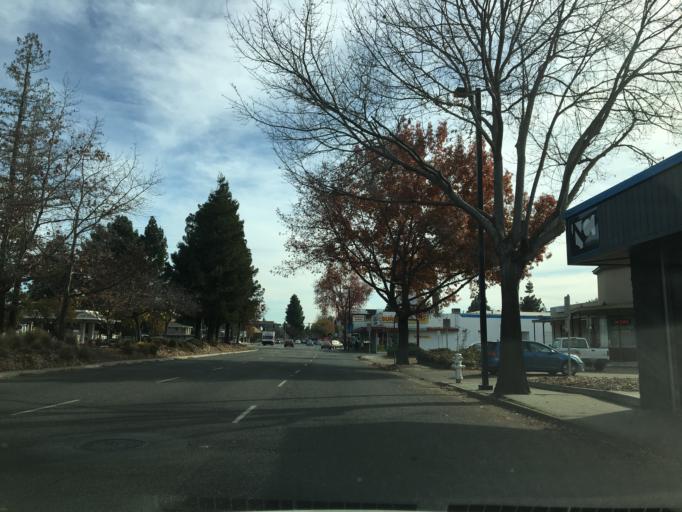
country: US
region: California
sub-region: Santa Clara County
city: Mountain View
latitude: 37.3887
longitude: -122.0900
